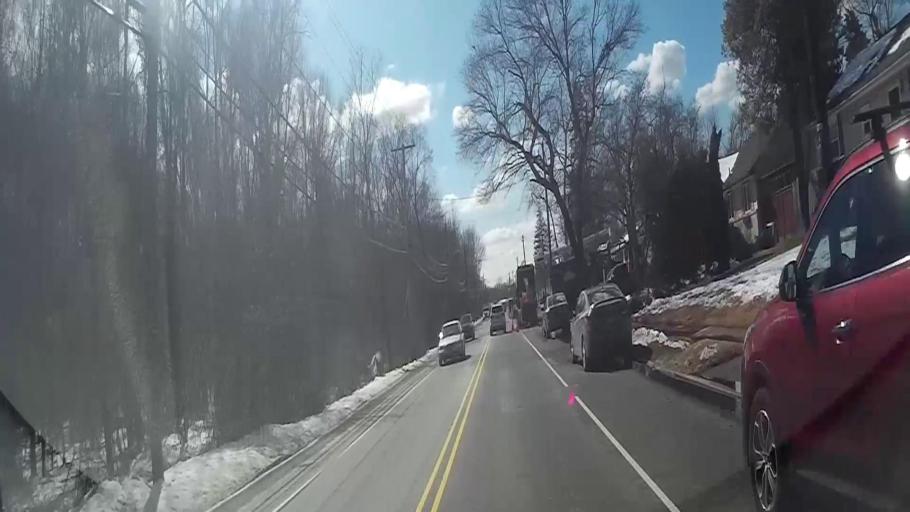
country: US
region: New Jersey
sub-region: Burlington County
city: Marlton
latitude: 39.8854
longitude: -74.8988
